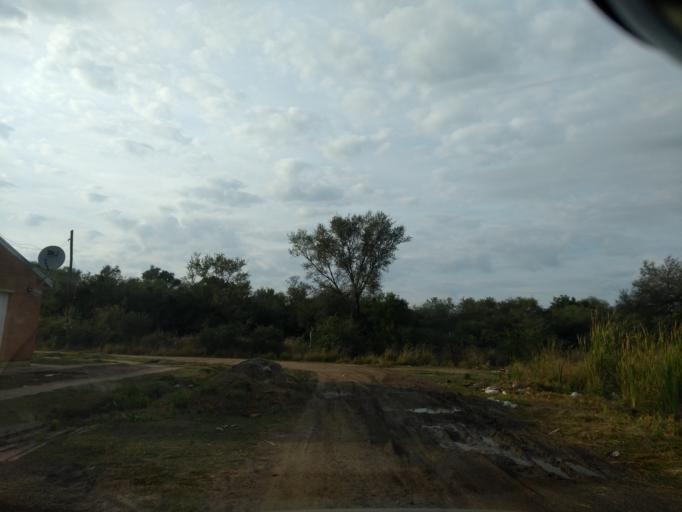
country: AR
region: Chaco
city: Fontana
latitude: -27.4241
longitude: -59.0502
